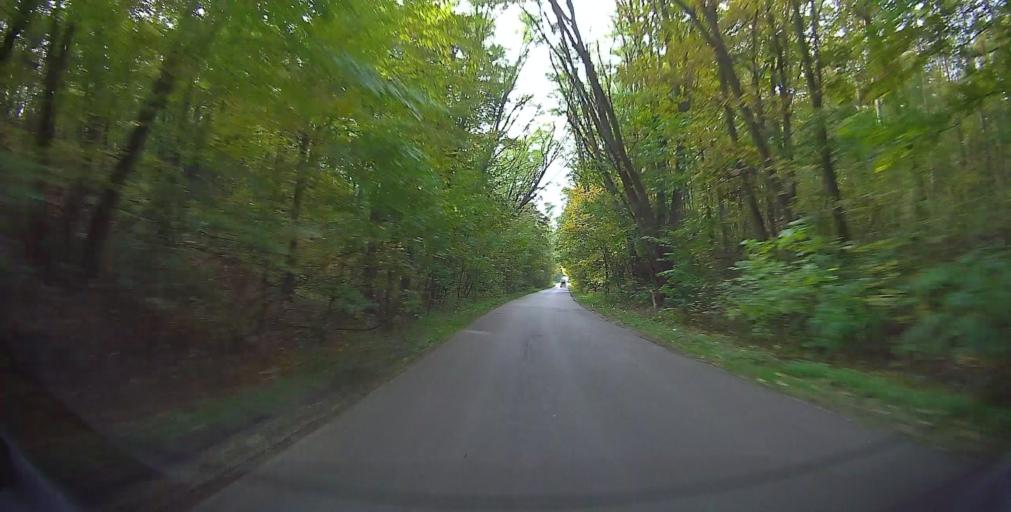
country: PL
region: Masovian Voivodeship
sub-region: Powiat grojecki
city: Mogielnica
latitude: 51.6451
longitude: 20.7554
